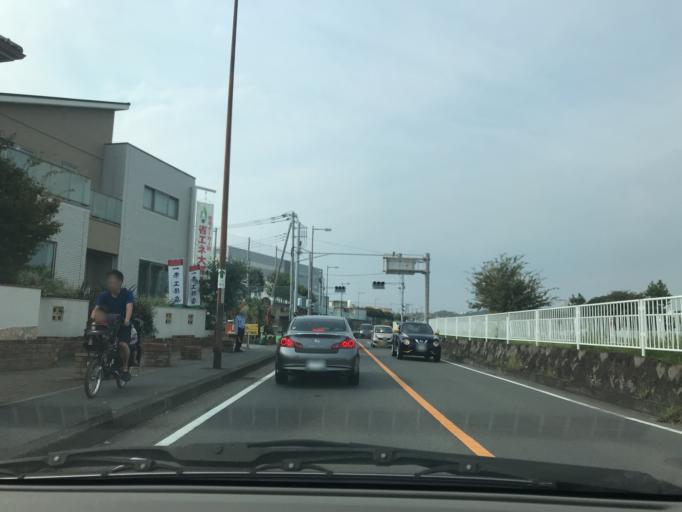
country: JP
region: Kanagawa
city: Fujisawa
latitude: 35.3392
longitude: 139.4678
